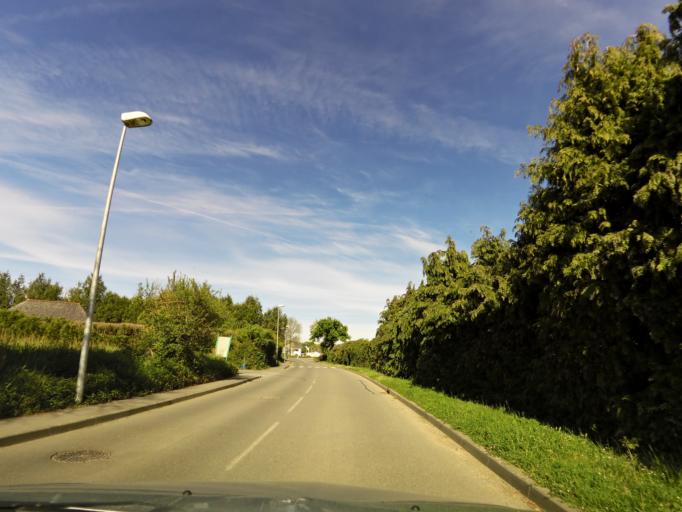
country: FR
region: Brittany
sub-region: Departement d'Ille-et-Vilaine
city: Bain-de-Bretagne
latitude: 47.8484
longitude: -1.6771
